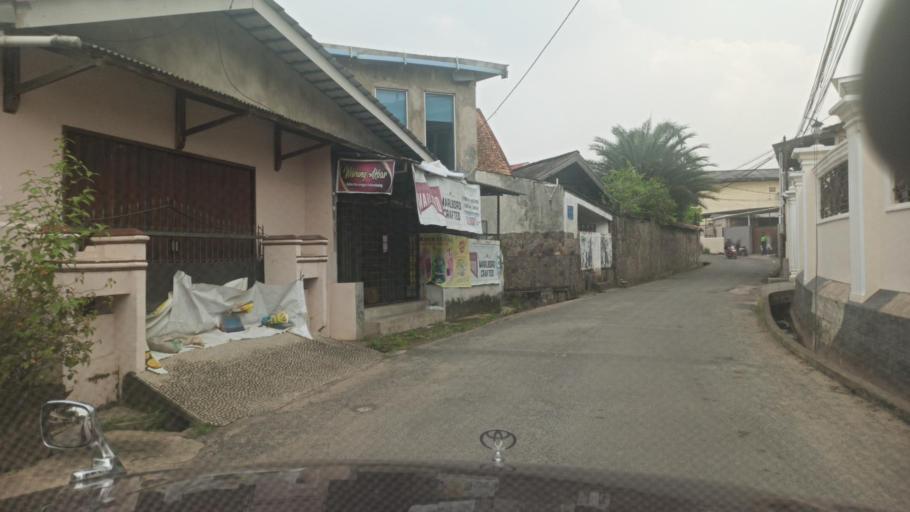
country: ID
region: South Sumatra
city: Plaju
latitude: -2.9917
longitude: 104.7401
